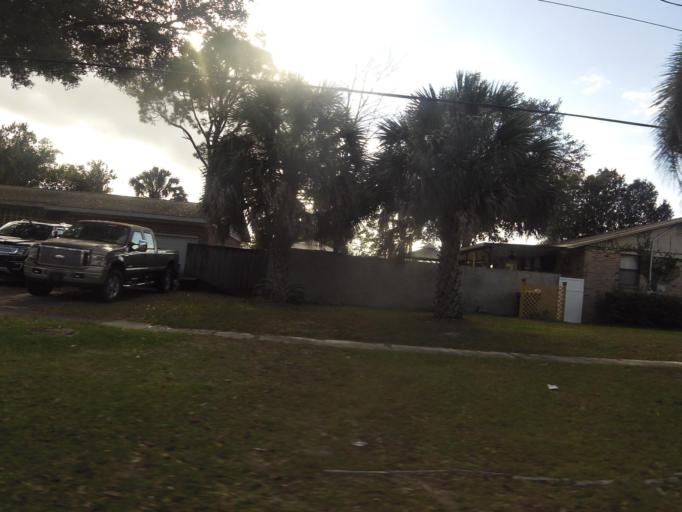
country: US
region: Florida
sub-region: Duval County
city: Jacksonville
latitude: 30.3396
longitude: -81.5756
